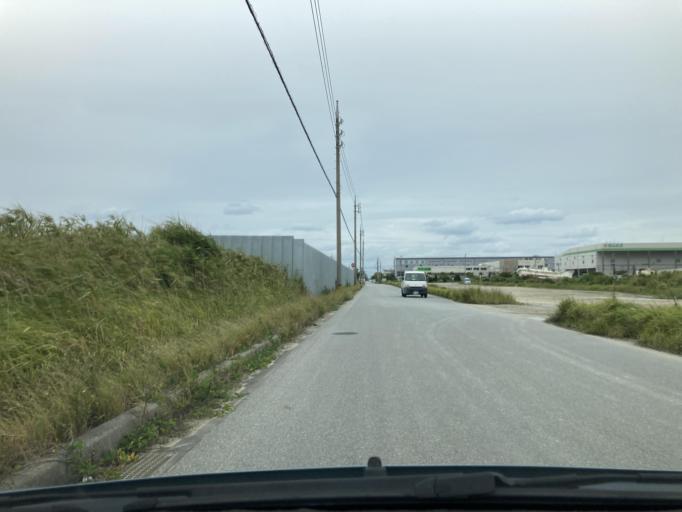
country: JP
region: Okinawa
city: Itoman
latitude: 26.1335
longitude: 127.6533
